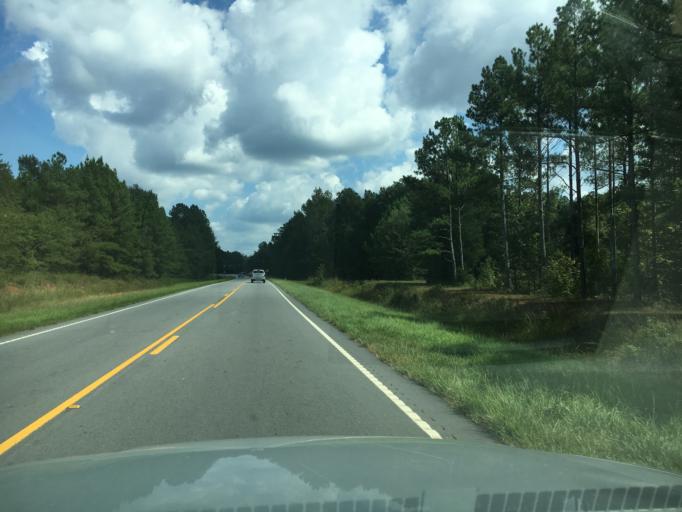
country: US
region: South Carolina
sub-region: Greenwood County
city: Greenwood
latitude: 34.1375
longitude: -82.1352
